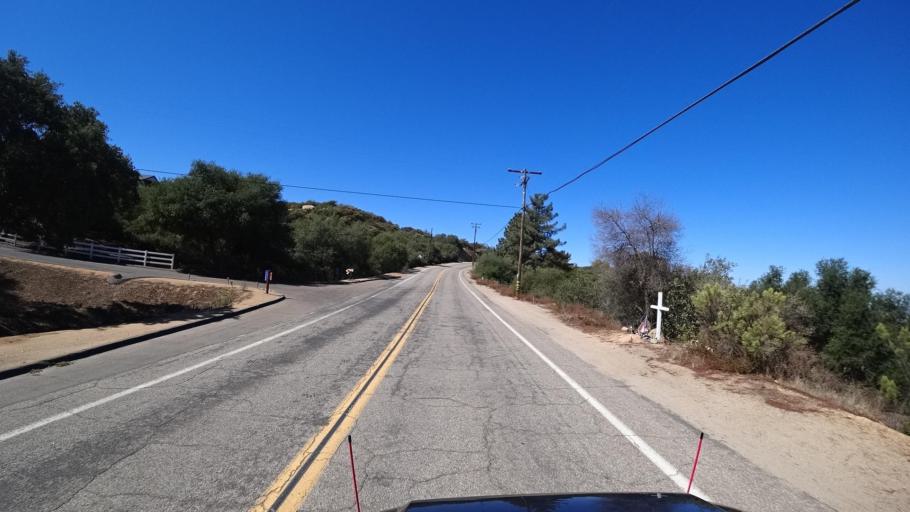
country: US
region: California
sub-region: San Diego County
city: Alpine
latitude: 32.7254
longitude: -116.7652
